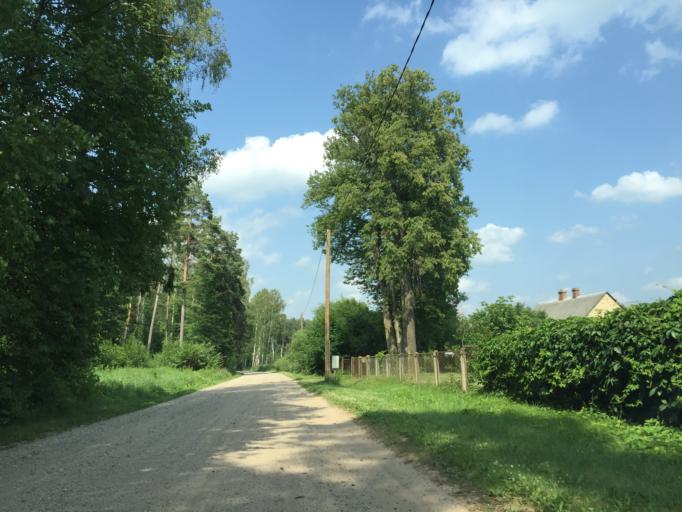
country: LV
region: Ozolnieku
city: Ozolnieki
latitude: 56.6726
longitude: 23.7561
